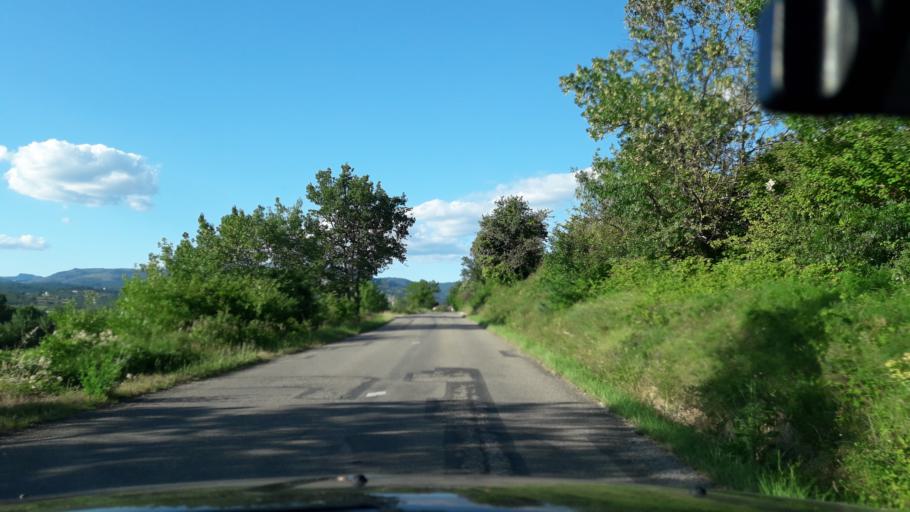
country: FR
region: Rhone-Alpes
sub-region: Departement de l'Ardeche
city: Lavilledieu
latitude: 44.6014
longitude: 4.4654
